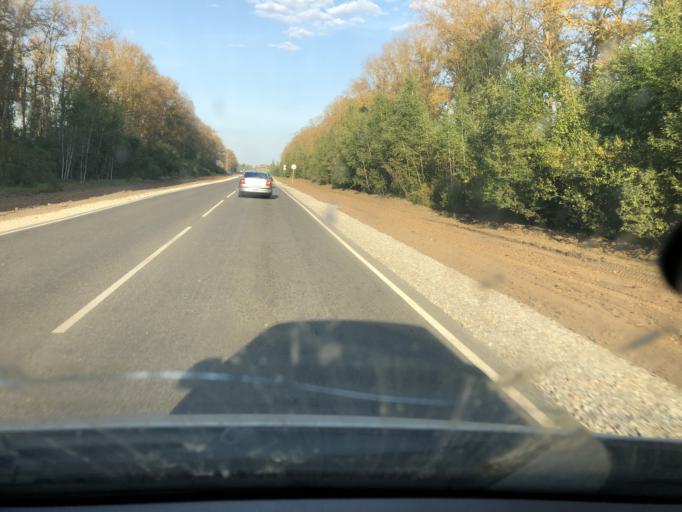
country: RU
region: Kaluga
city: Peremyshl'
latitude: 54.2521
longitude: 36.1151
